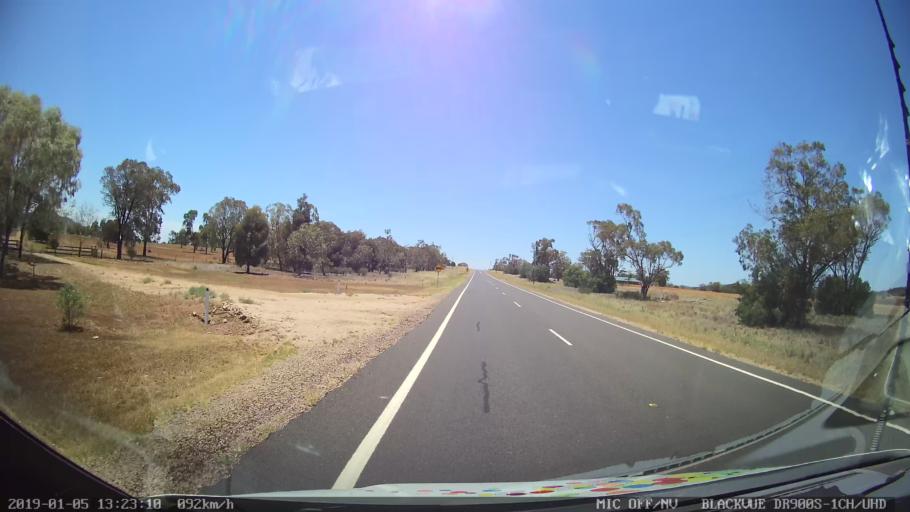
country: AU
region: New South Wales
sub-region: Gunnedah
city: Gunnedah
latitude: -31.0801
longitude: 149.9717
